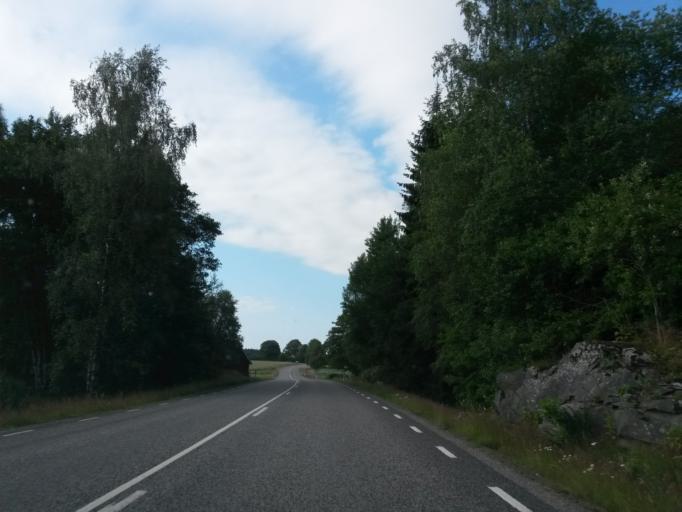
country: SE
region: Vaestra Goetaland
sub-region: Vargarda Kommun
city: Jonstorp
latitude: 58.0444
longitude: 12.6510
